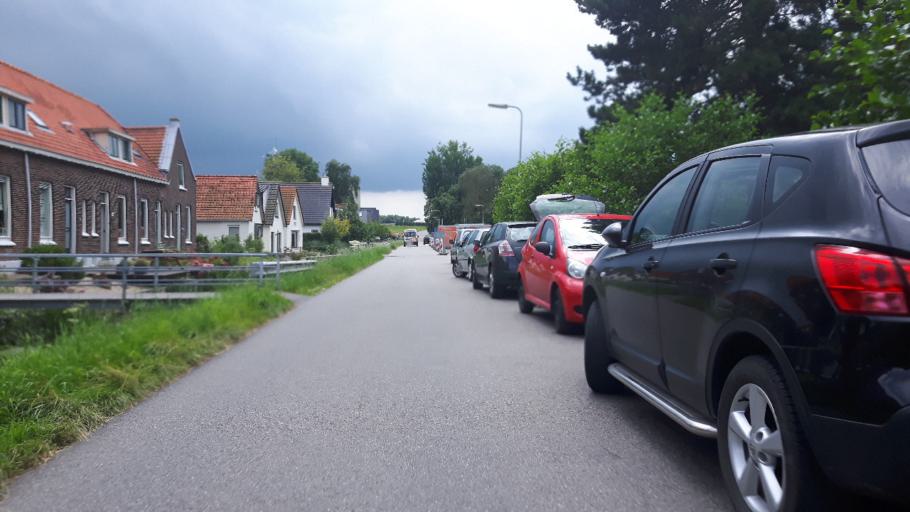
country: NL
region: South Holland
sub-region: Molenwaard
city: Liesveld
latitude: 51.9237
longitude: 4.7854
